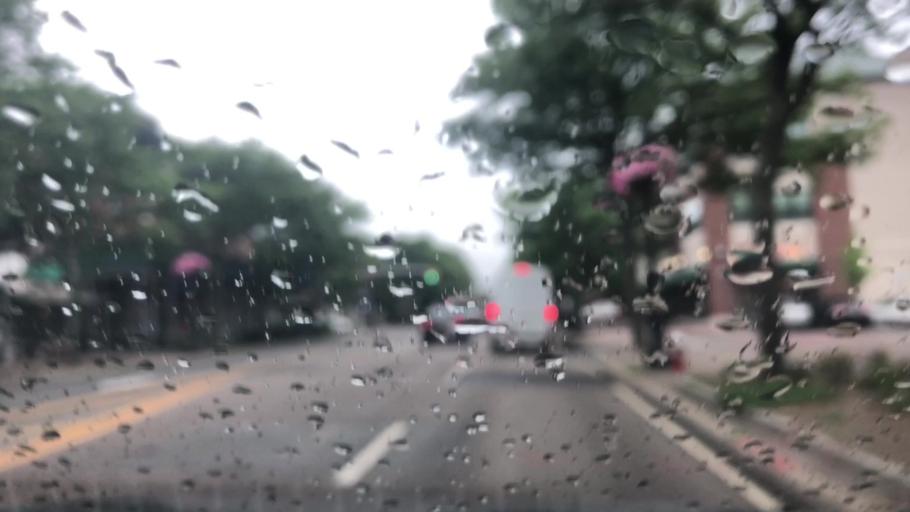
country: US
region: New York
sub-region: Nassau County
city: Garden City
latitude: 40.7261
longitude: -73.6344
